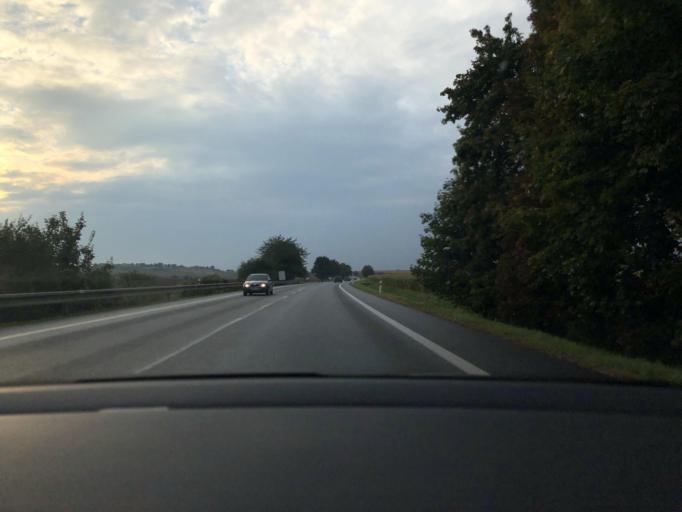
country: CZ
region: Central Bohemia
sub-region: Okres Kolin
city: Kolin
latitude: 50.0340
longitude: 15.1583
